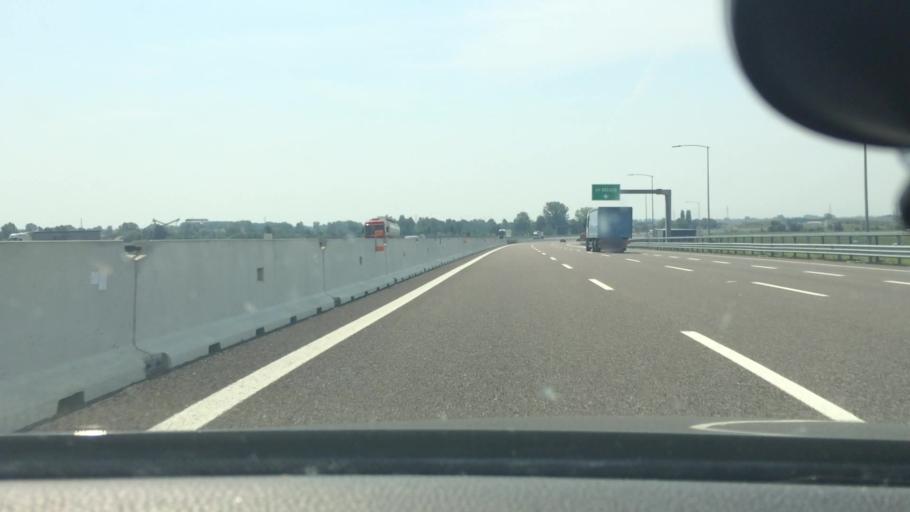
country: IT
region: Lombardy
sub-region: Citta metropolitana di Milano
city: Pozzuolo Martesana
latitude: 45.5034
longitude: 9.4435
